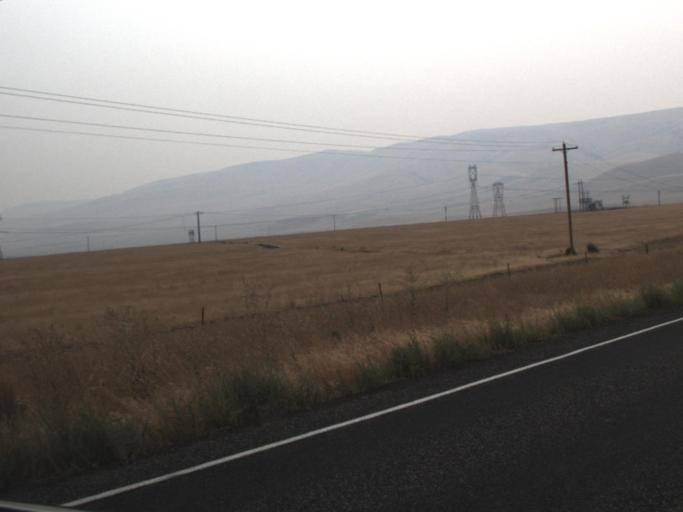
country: US
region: Washington
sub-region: Grant County
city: Desert Aire
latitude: 46.5188
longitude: -119.8742
